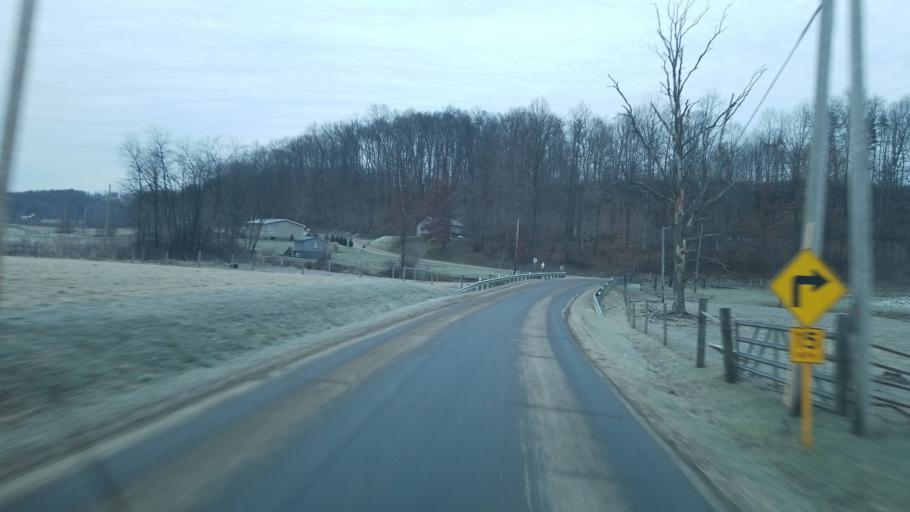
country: US
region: Ohio
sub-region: Holmes County
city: Millersburg
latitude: 40.4847
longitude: -81.8582
